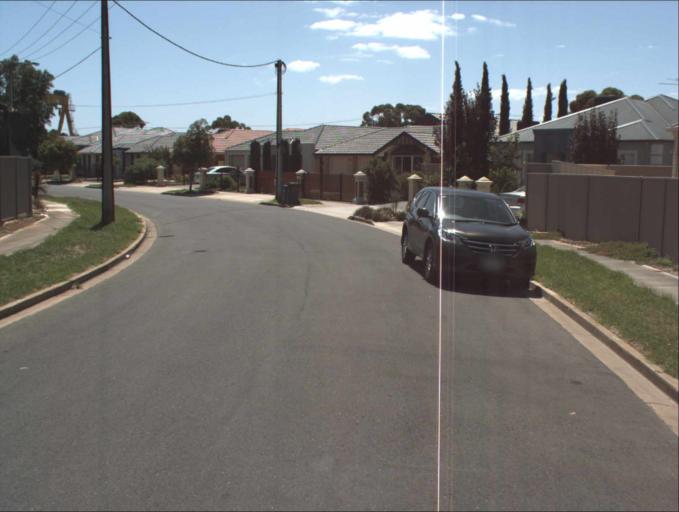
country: AU
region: South Australia
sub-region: Charles Sturt
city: Woodville North
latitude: -34.8555
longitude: 138.5613
